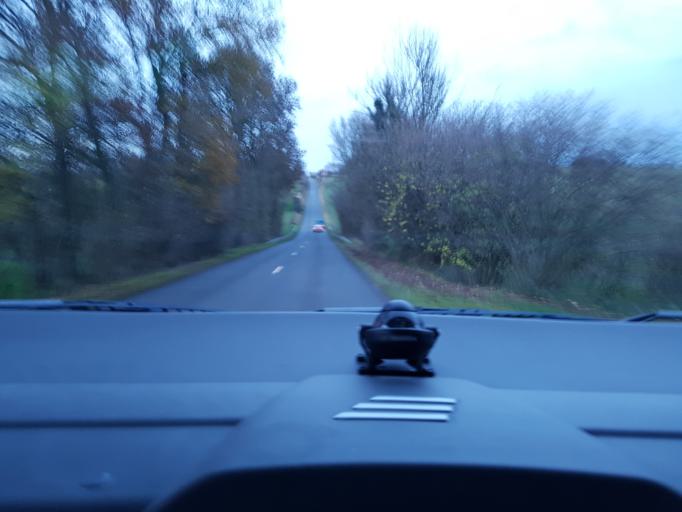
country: FR
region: Picardie
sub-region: Departement de la Somme
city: Beauquesne
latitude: 50.0462
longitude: 2.4066
